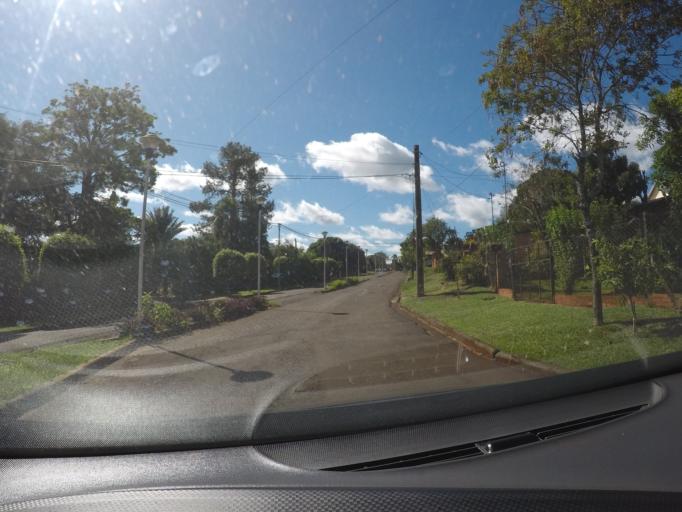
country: AR
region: Misiones
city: Puerto Rico
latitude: -26.7984
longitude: -55.0204
